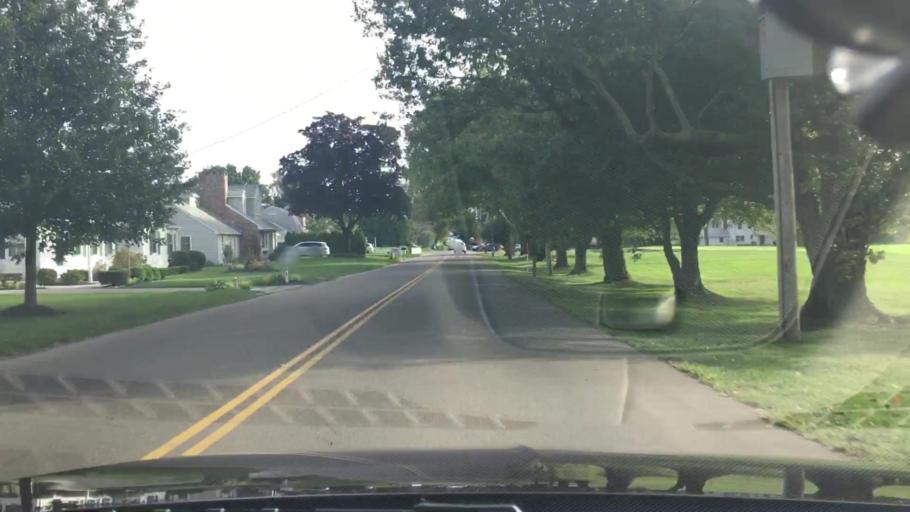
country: US
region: Connecticut
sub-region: New Haven County
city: Madison Center
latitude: 41.2742
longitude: -72.6077
